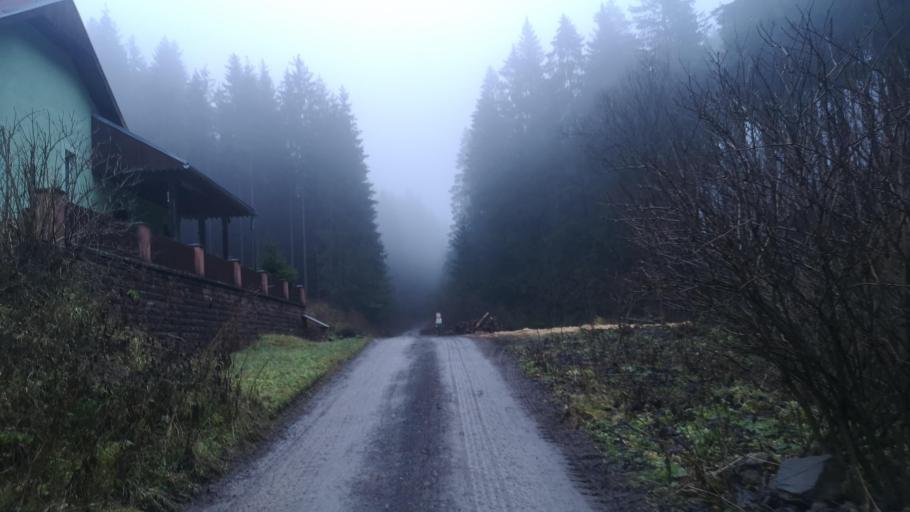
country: SK
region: Banskobystricky
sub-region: Okres Ziar nad Hronom
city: Kremnica
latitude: 48.7549
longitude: 18.9362
